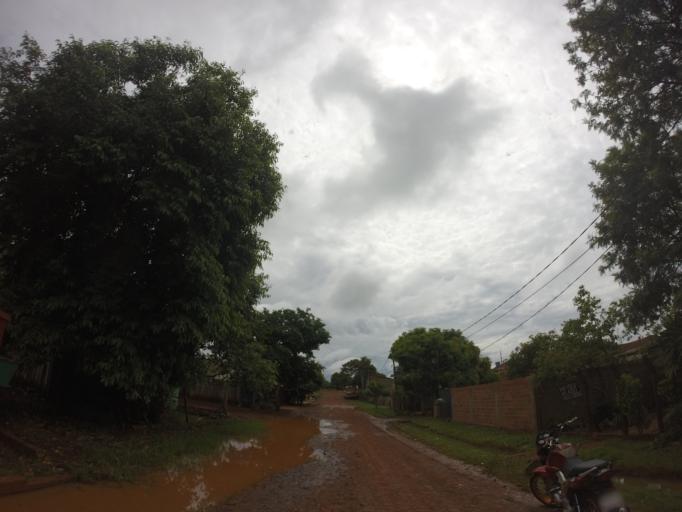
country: PY
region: Alto Parana
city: Ciudad del Este
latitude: -25.3997
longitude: -54.6343
